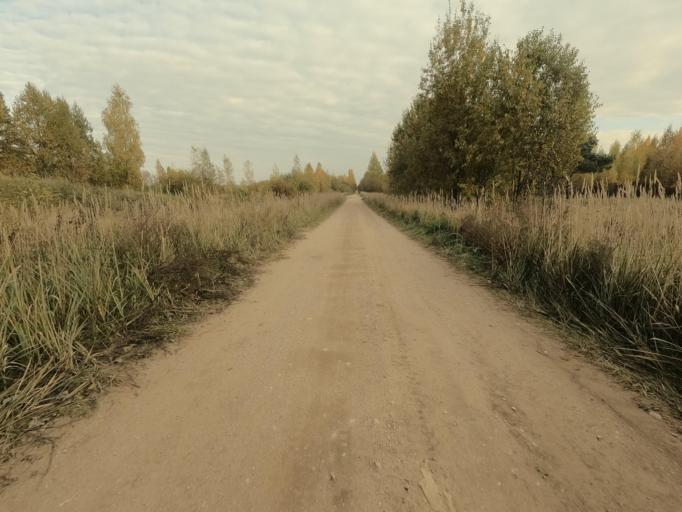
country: RU
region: Novgorod
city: Pankovka
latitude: 58.8981
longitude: 30.9946
